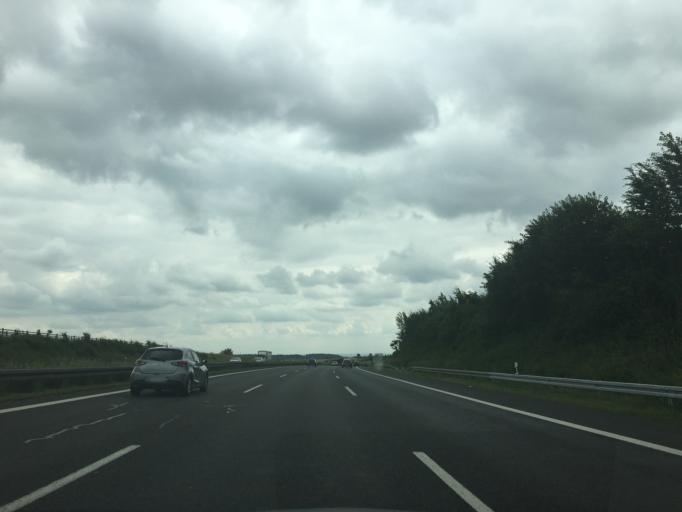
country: DE
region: Bavaria
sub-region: Upper Bavaria
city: Stammham
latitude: 48.8755
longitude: 11.4679
